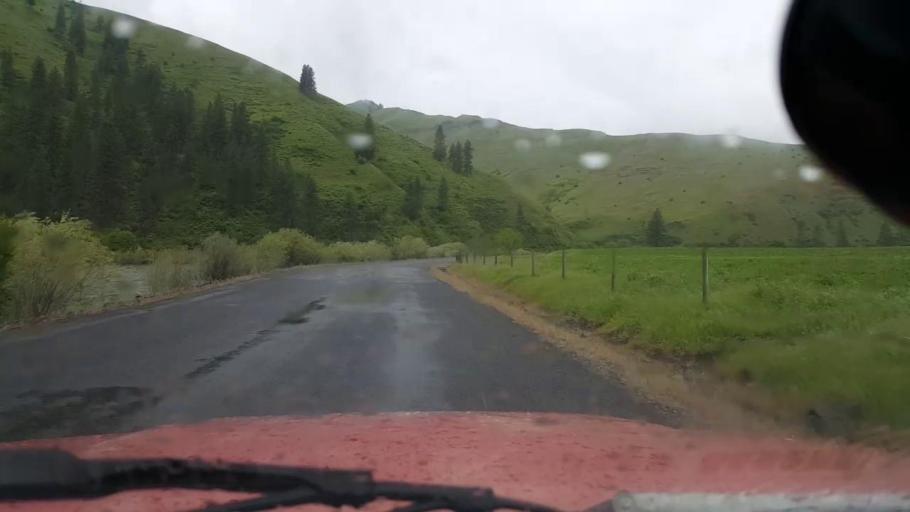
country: US
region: Washington
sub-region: Asotin County
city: Asotin
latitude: 46.0291
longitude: -117.3069
